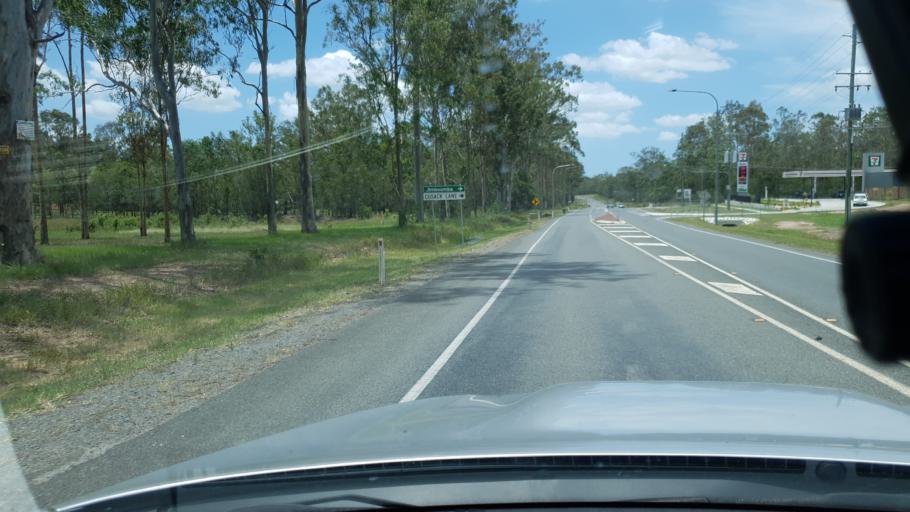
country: AU
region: Queensland
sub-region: Logan
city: North Maclean
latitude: -27.8130
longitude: 152.9764
